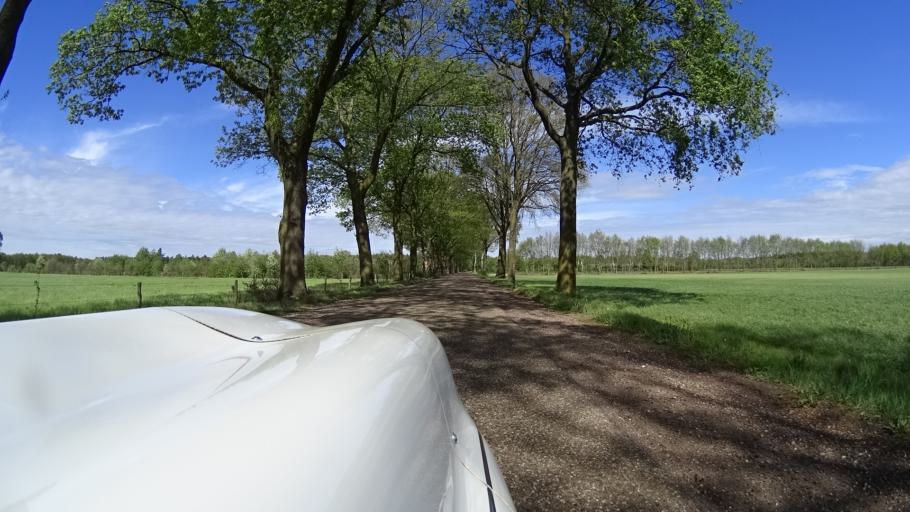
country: NL
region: North Brabant
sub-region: Gemeente Mill en Sint Hubert
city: Wilbertoord
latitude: 51.5936
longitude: 5.8139
